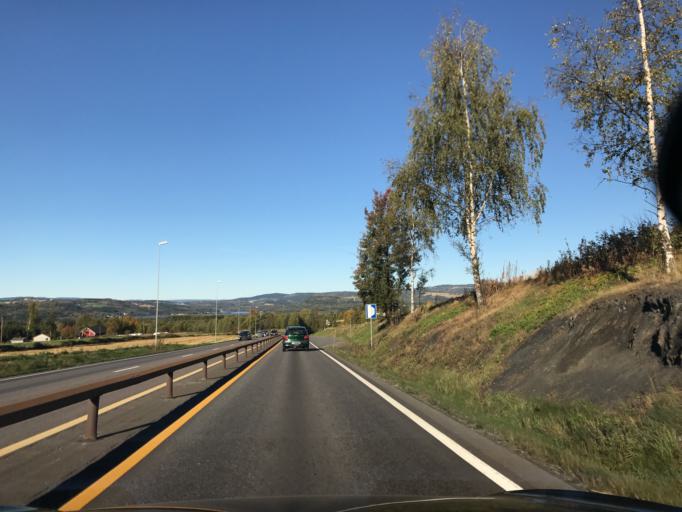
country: NO
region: Hedmark
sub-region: Ringsaker
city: Brumunddal
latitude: 60.8577
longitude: 10.9764
